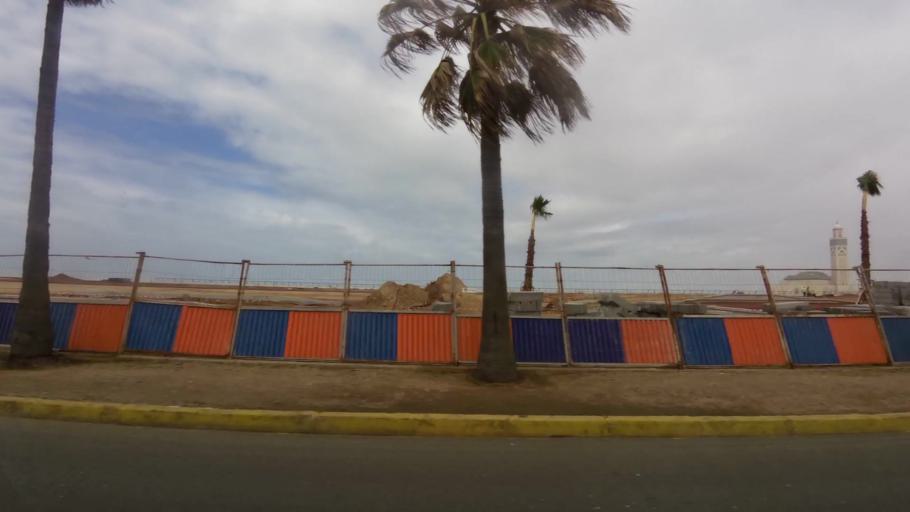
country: MA
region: Grand Casablanca
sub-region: Casablanca
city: Casablanca
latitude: 33.6054
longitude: -7.6477
